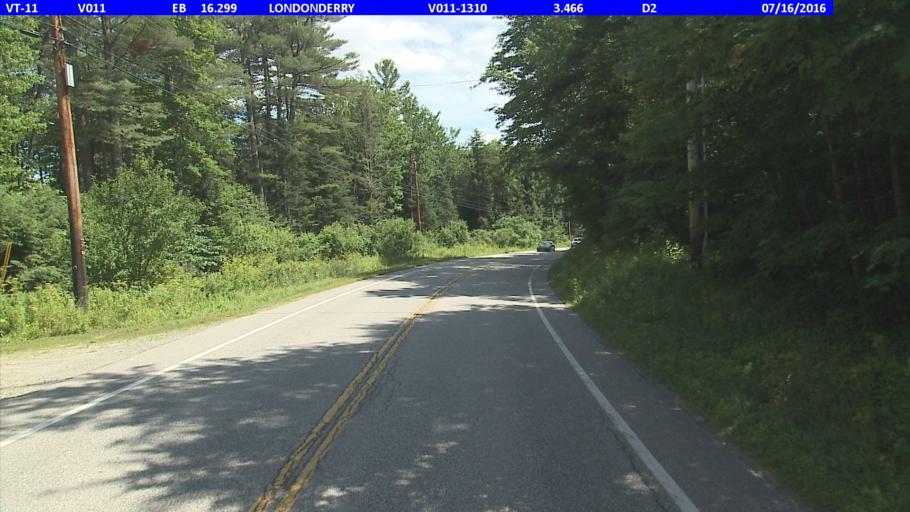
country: US
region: Vermont
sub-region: Windsor County
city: Chester
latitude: 43.2180
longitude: -72.7911
